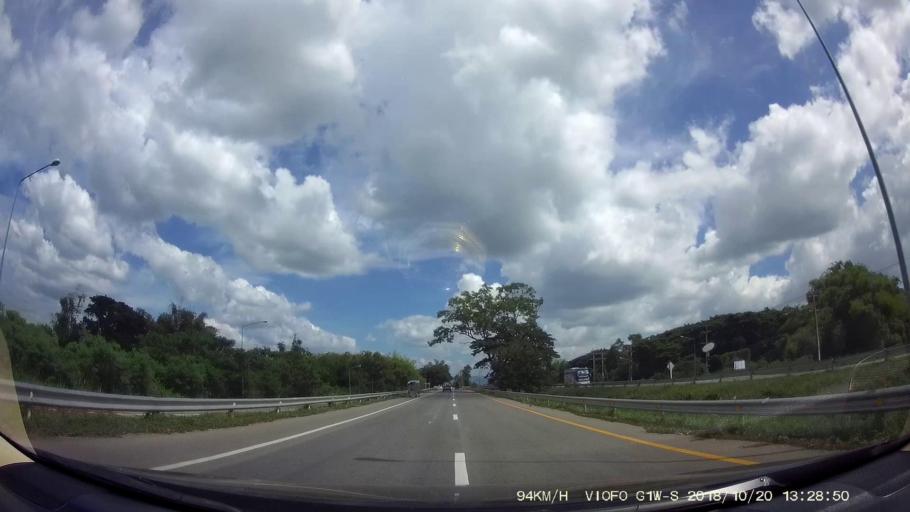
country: TH
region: Chaiyaphum
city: Khon San
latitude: 16.5909
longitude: 101.9812
